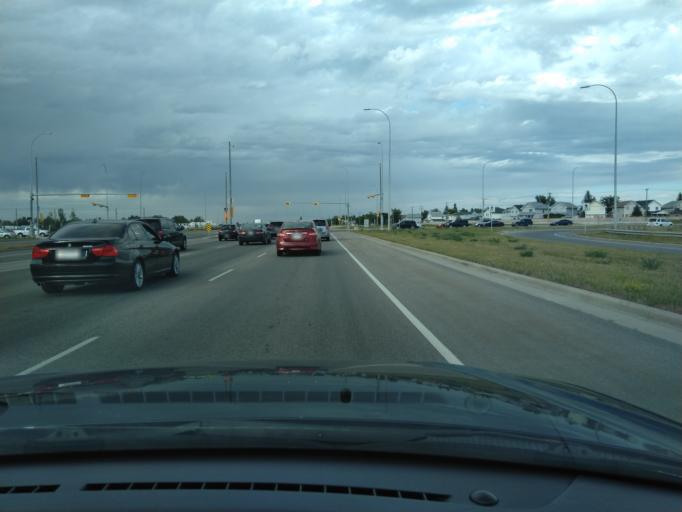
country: CA
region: Alberta
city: Calgary
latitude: 51.1110
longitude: -113.9747
